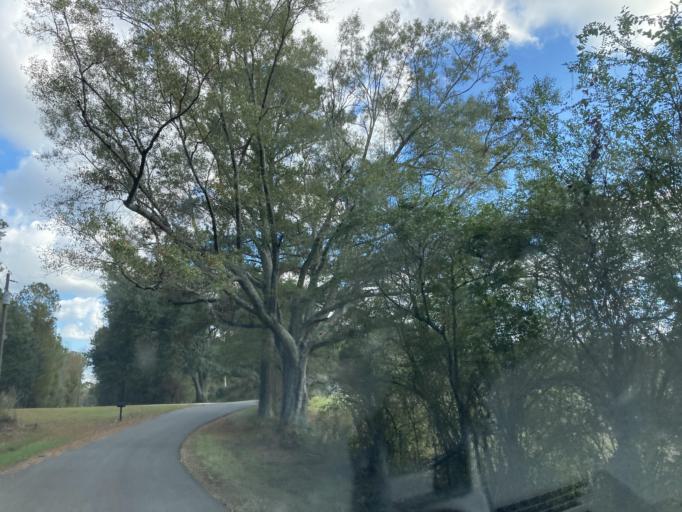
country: US
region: Mississippi
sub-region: Lamar County
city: Sumrall
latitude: 31.3756
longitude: -89.5465
